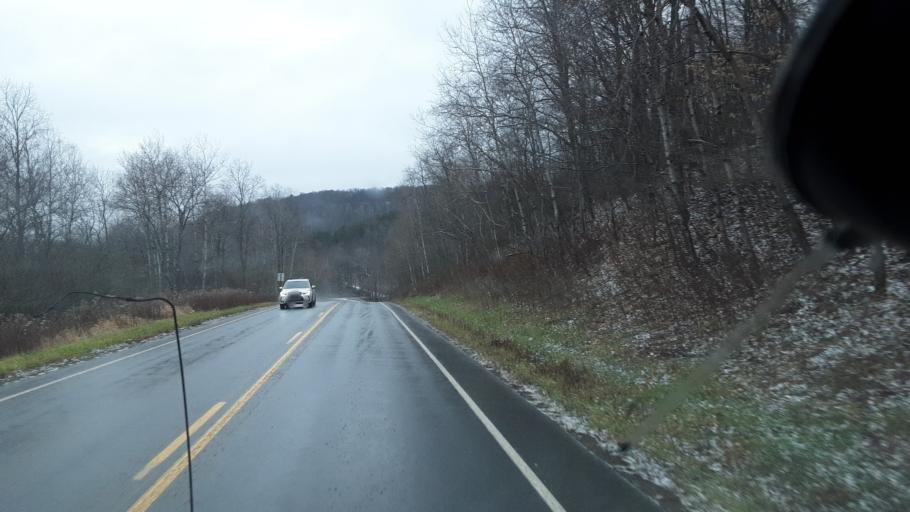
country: US
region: Pennsylvania
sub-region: Potter County
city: Coudersport
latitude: 41.8346
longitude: -77.9165
